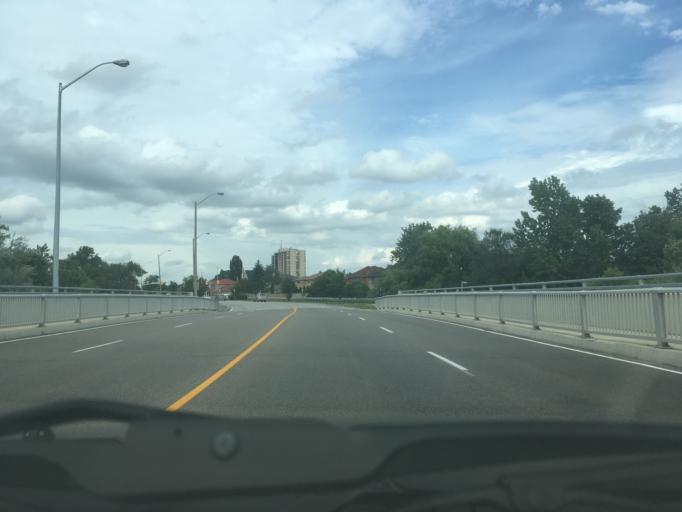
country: CA
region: Ontario
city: Brampton
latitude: 43.6535
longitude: -79.7295
